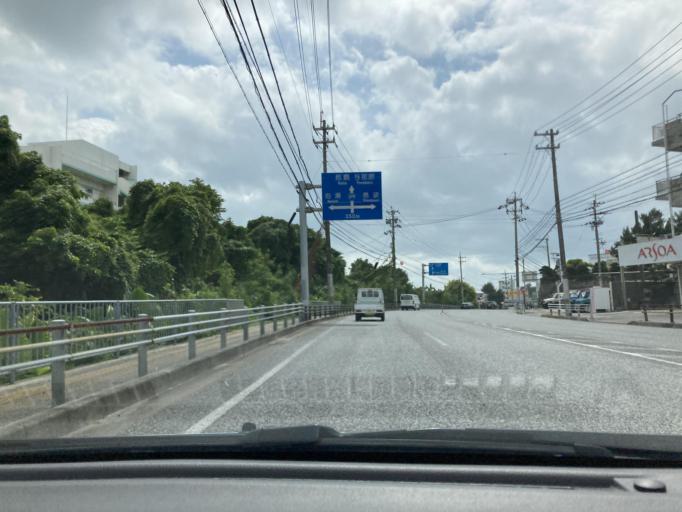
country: JP
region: Okinawa
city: Okinawa
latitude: 26.3217
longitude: 127.8217
